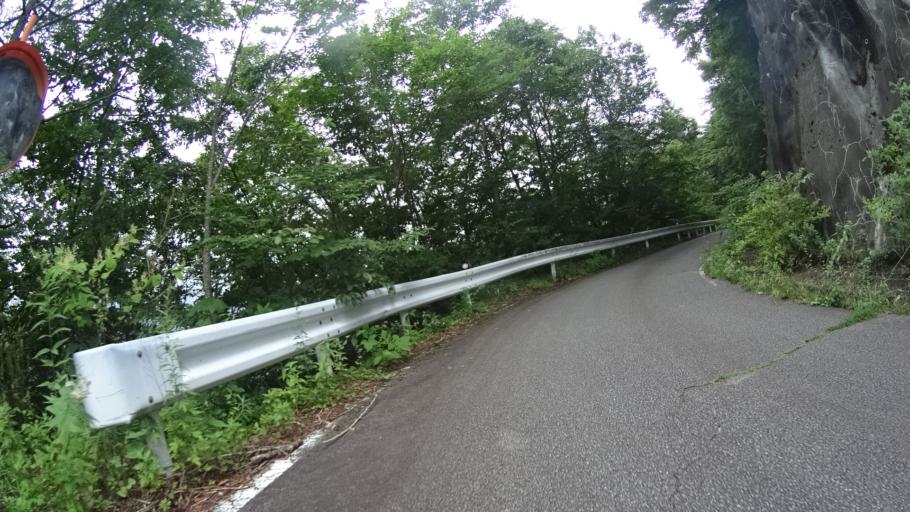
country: JP
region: Yamanashi
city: Enzan
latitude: 35.8092
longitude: 138.6231
